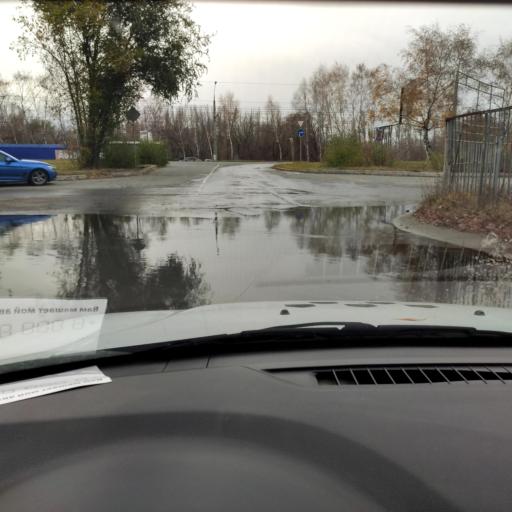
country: RU
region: Samara
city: Tol'yatti
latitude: 53.5522
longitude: 49.3085
